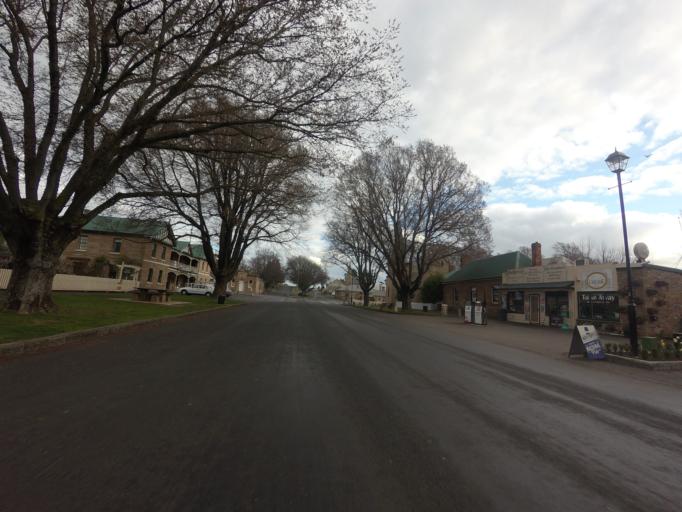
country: AU
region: Tasmania
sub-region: Northern Midlands
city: Evandale
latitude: -42.0303
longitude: 147.4923
